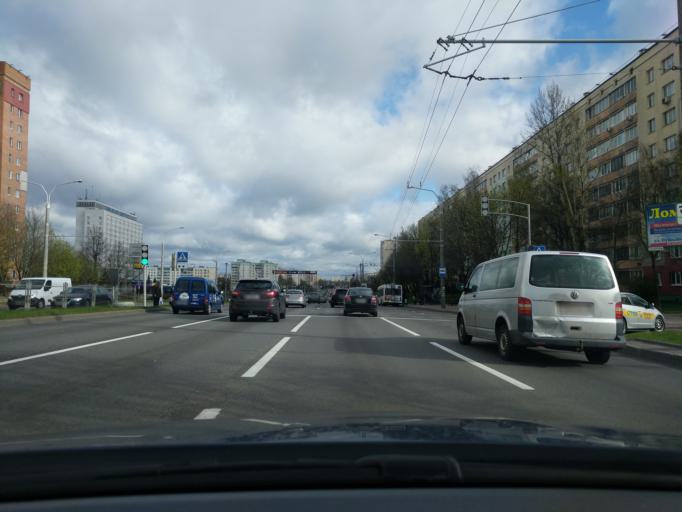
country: BY
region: Minsk
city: Novoye Medvezhino
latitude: 53.9055
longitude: 27.4963
